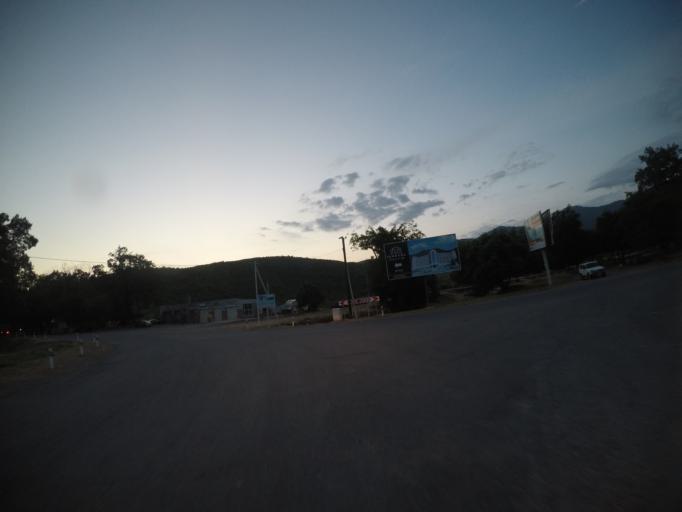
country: AZ
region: Oguz
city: Oguz
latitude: 41.0527
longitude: 47.4227
